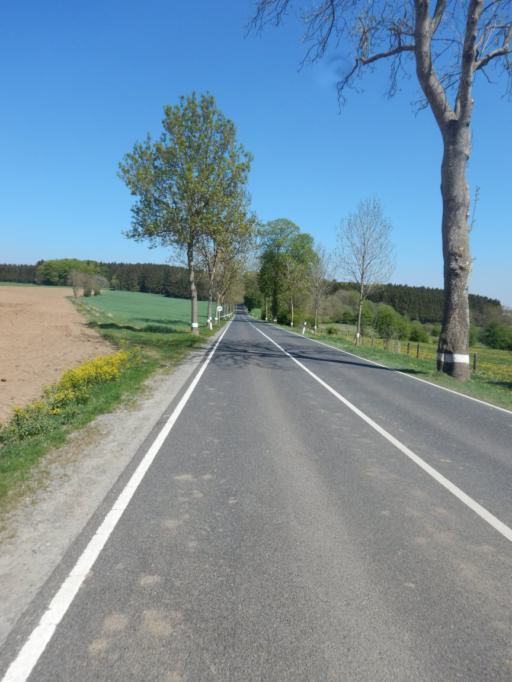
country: LU
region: Diekirch
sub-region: Canton de Clervaux
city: Troisvierges
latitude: 50.1474
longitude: 6.0325
